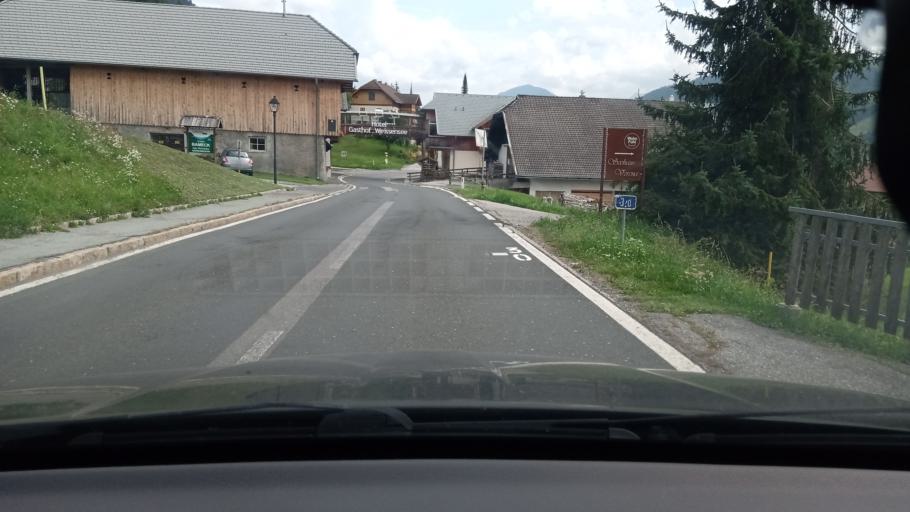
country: AT
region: Carinthia
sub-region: Politischer Bezirk Spittal an der Drau
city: Steinfeld
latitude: 46.7208
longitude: 13.2785
